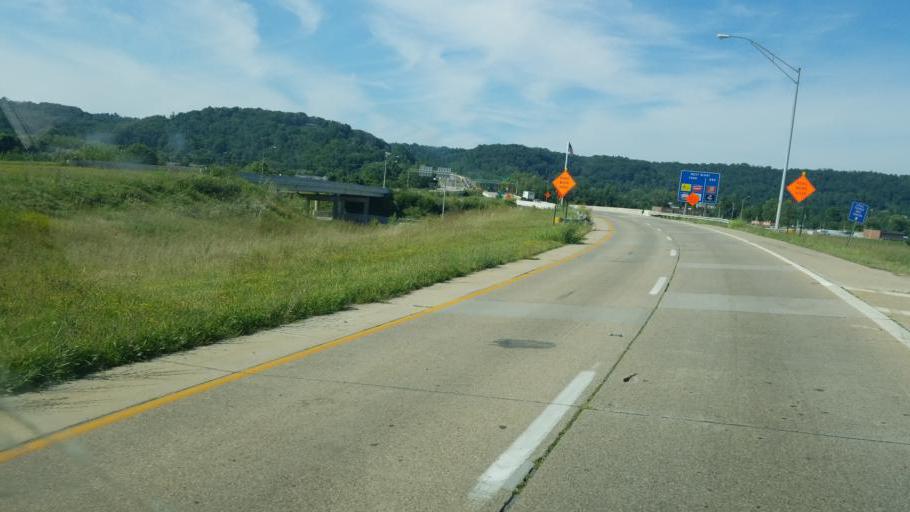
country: US
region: Ohio
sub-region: Athens County
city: Athens
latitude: 39.3301
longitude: -82.0827
